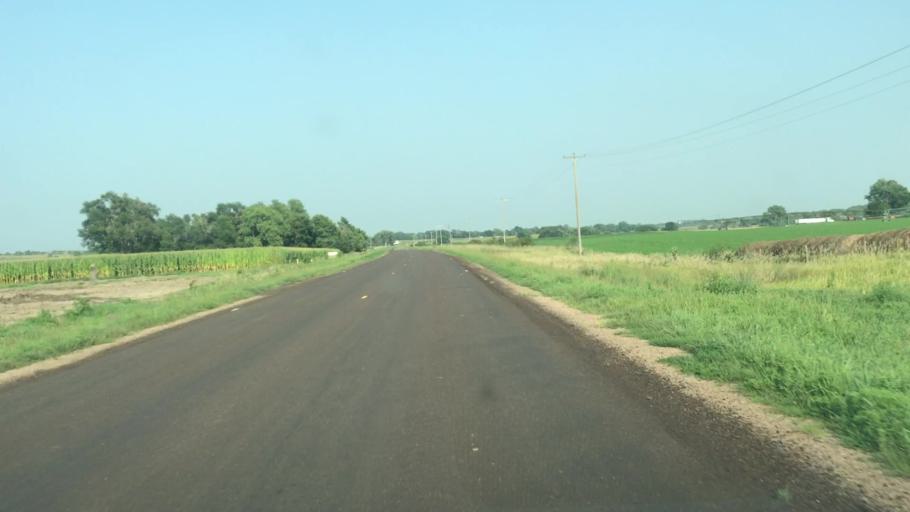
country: US
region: Nebraska
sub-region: Buffalo County
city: Ravenna
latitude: 41.0756
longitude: -98.7403
